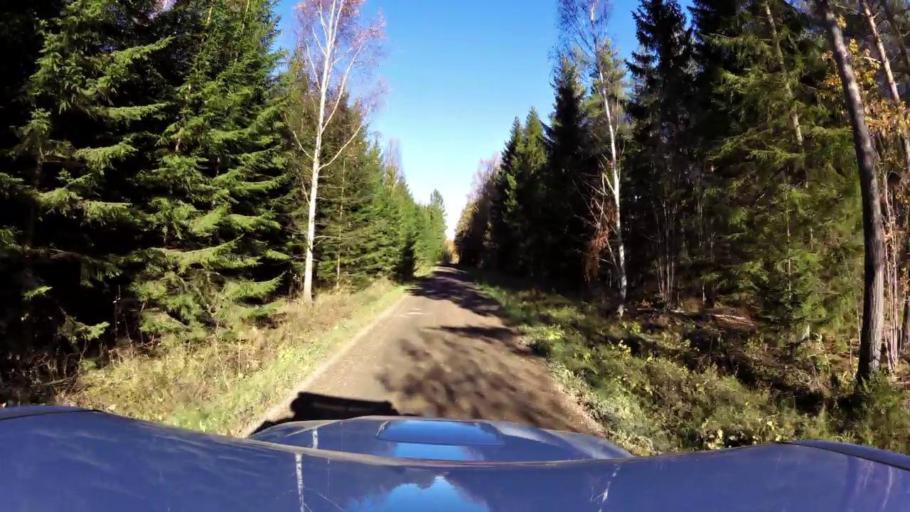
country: SE
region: OEstergoetland
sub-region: Linkopings Kommun
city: Ljungsbro
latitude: 58.4962
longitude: 15.3865
